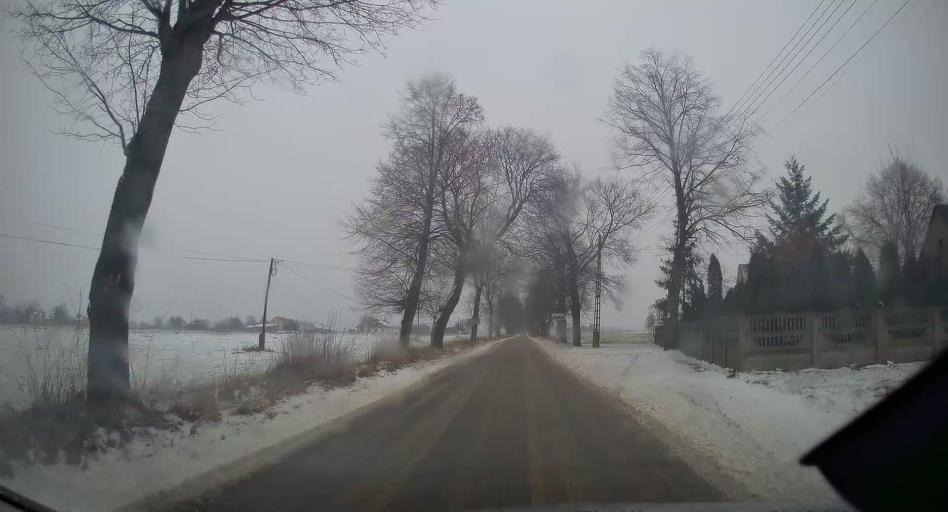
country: PL
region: Lodz Voivodeship
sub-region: Powiat tomaszowski
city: Czerniewice
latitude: 51.6794
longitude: 20.2189
